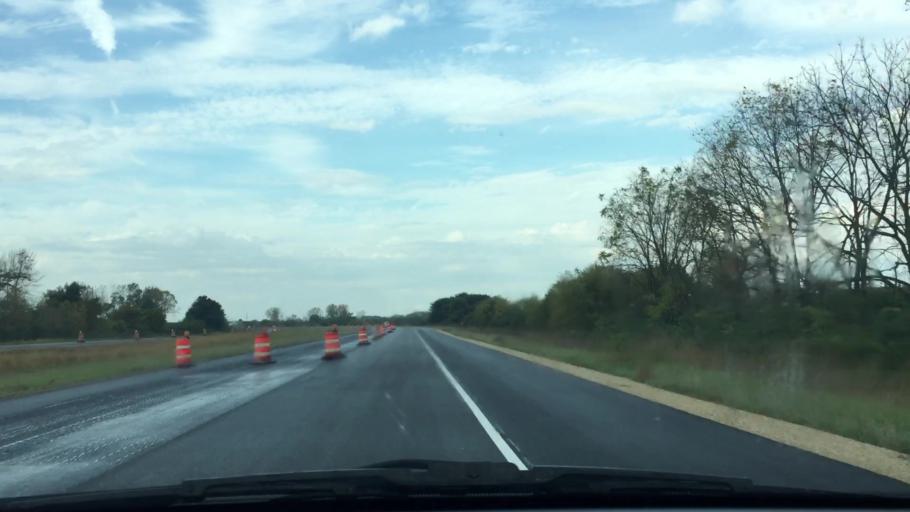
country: US
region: Illinois
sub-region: Whiteside County
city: Erie
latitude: 41.7066
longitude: -90.0435
